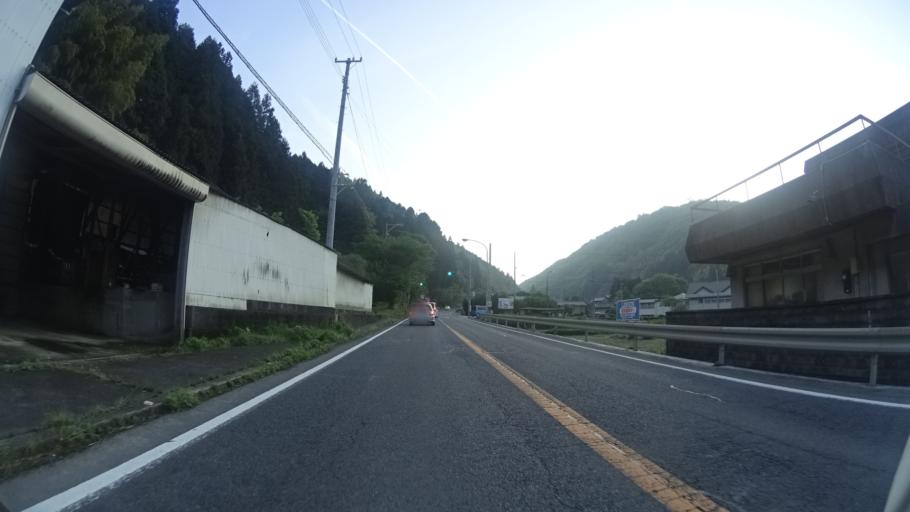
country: JP
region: Tokushima
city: Ikedacho
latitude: 34.0021
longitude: 133.7060
